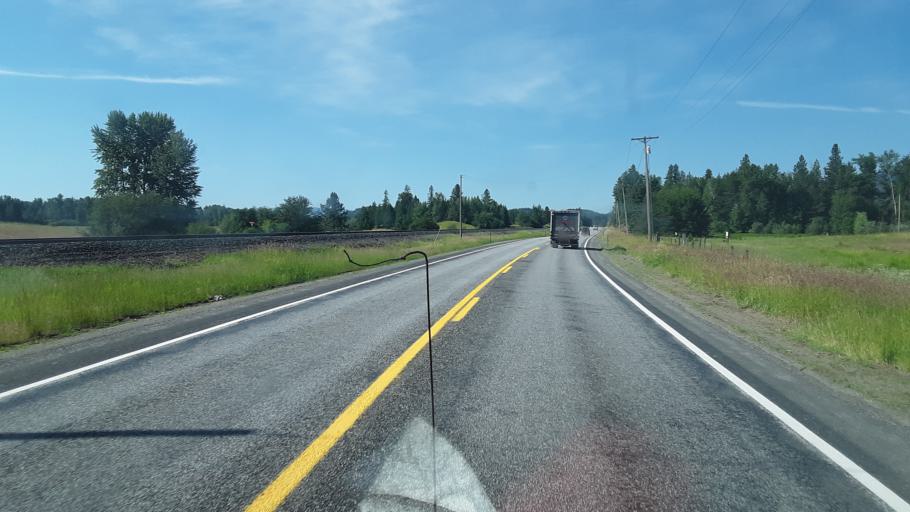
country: US
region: Idaho
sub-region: Bonner County
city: Ponderay
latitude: 48.4540
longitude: -116.4769
